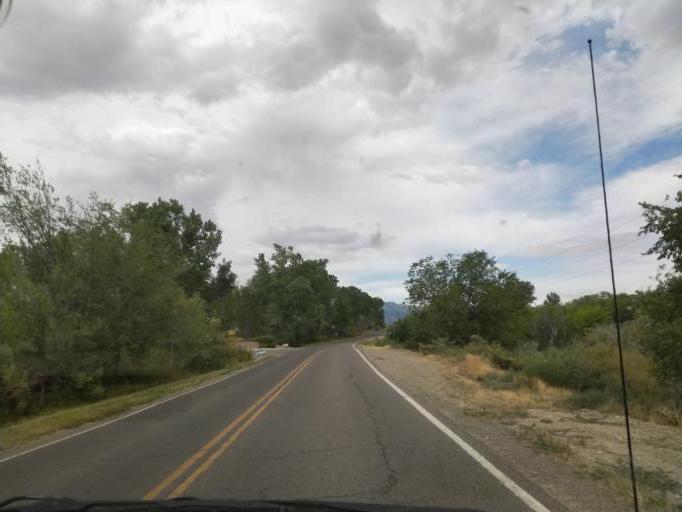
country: US
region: Colorado
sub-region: Mesa County
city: Clifton
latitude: 39.0559
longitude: -108.4419
